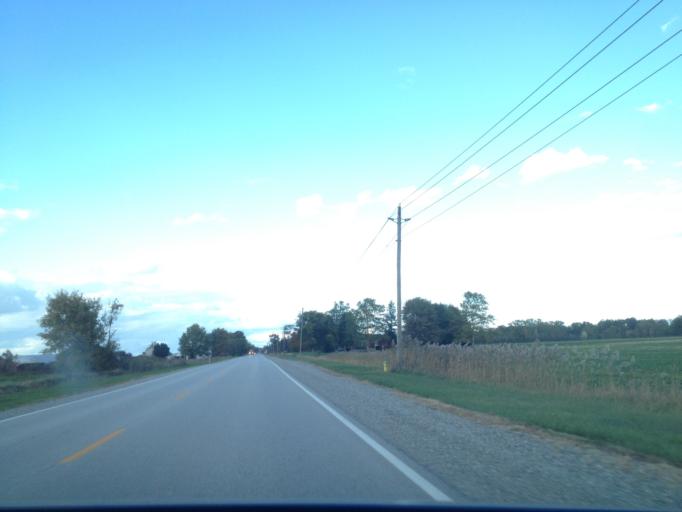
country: US
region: Michigan
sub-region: Wayne County
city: Grosse Pointe
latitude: 42.1537
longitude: -82.7322
